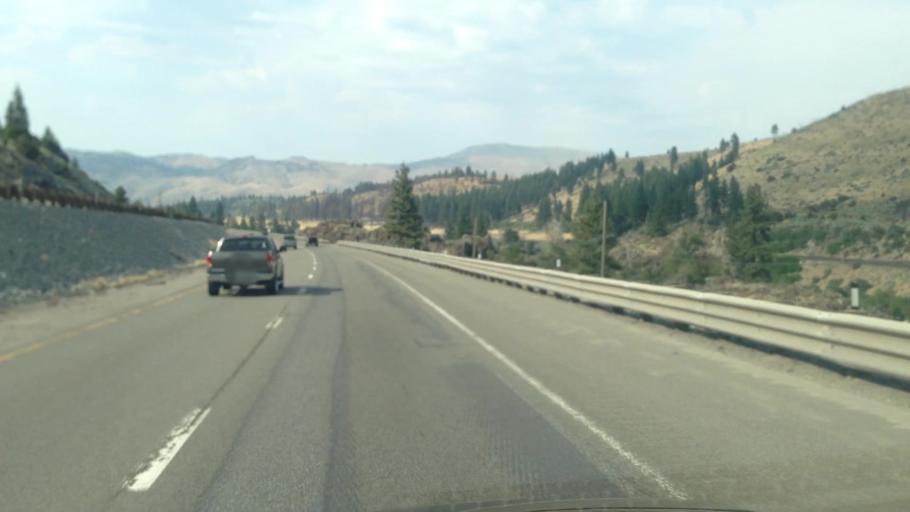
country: US
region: Nevada
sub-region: Washoe County
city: Verdi
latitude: 39.4804
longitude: -119.9953
